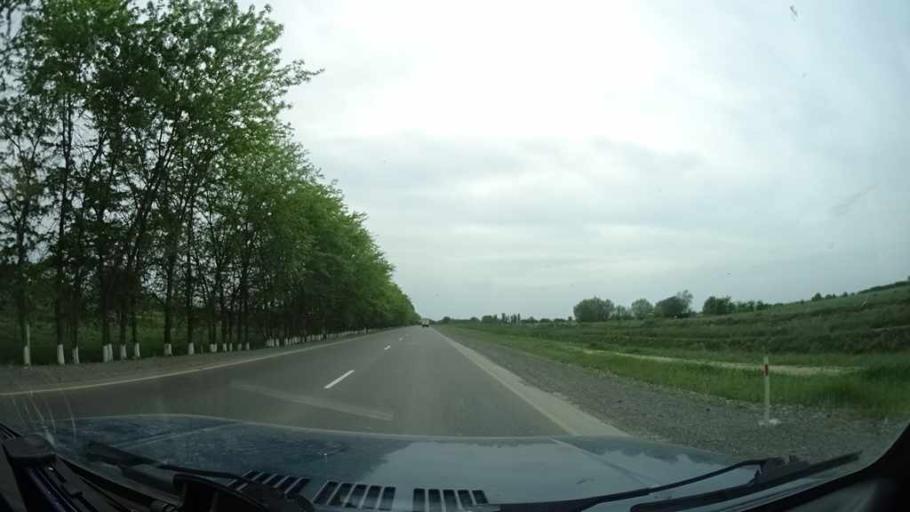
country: AZ
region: Aghjabadi Rayon
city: Agdzhabedy
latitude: 40.0401
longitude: 47.4077
